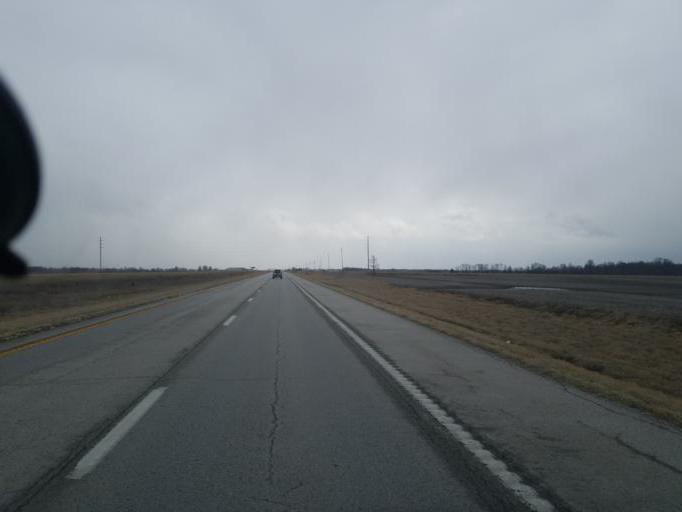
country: US
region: Missouri
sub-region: Randolph County
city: Moberly
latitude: 39.5580
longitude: -92.4583
